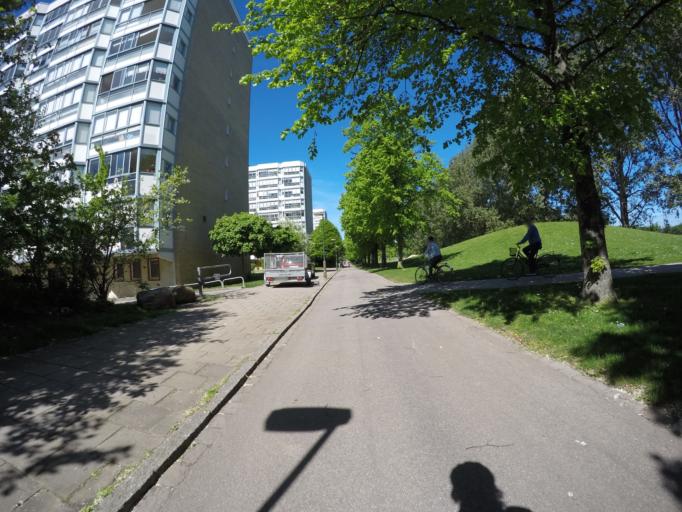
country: SE
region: Skane
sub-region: Burlovs Kommun
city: Arloev
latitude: 55.5885
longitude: 13.0491
